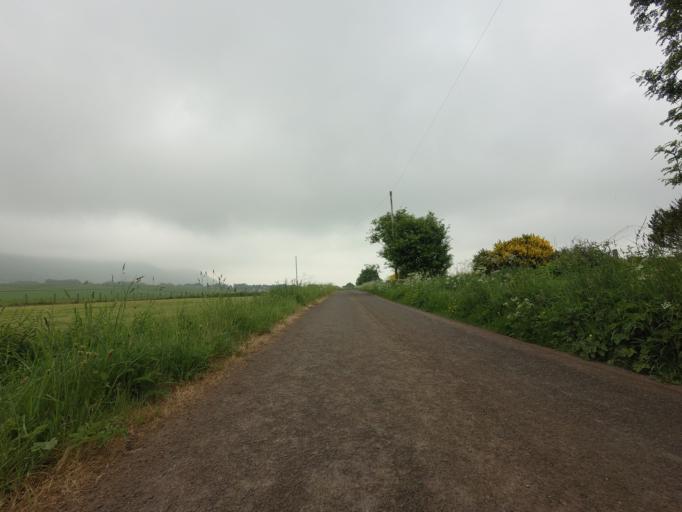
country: GB
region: Scotland
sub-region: Fife
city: Ballingry
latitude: 56.2372
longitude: -3.3441
